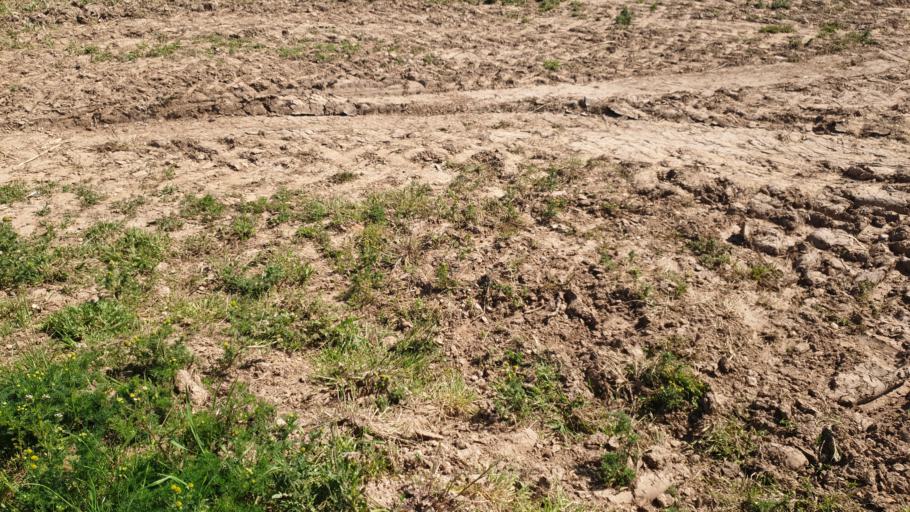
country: GB
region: England
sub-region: Essex
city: Great Bentley
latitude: 51.8598
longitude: 1.0471
